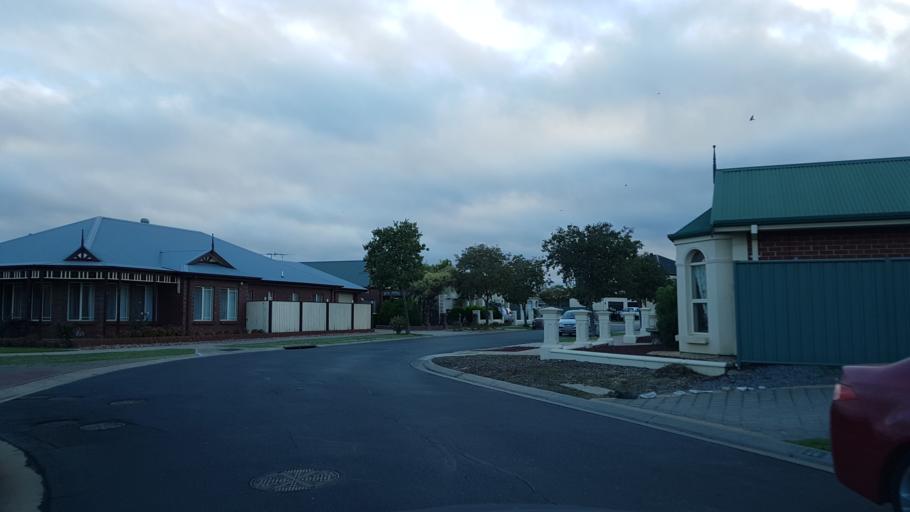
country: AU
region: South Australia
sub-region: Salisbury
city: Ingle Farm
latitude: -34.8116
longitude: 138.6065
